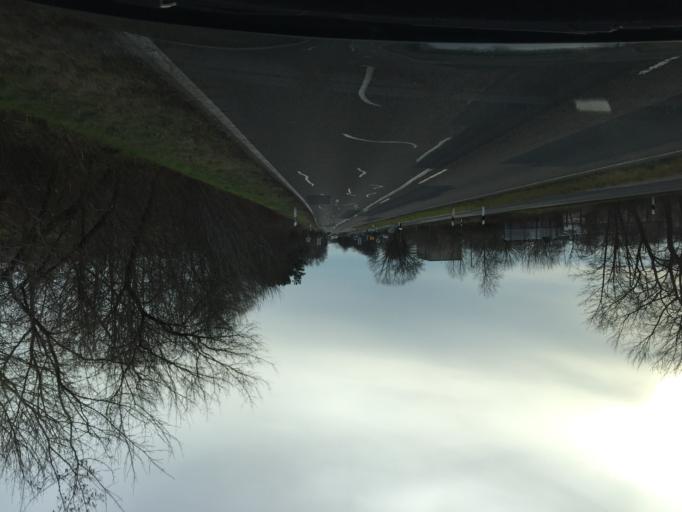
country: DE
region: Brandenburg
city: Cottbus
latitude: 51.7795
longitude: 14.3674
